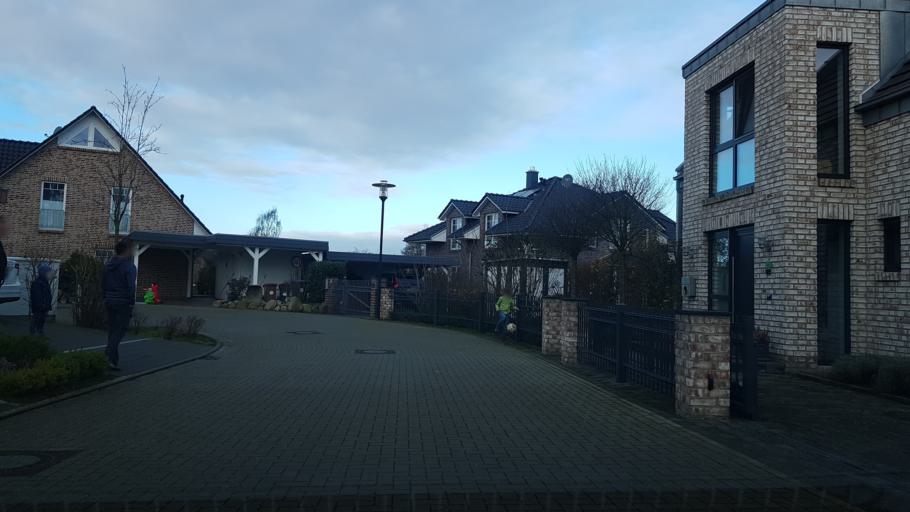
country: DE
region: Lower Saxony
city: Bardowick
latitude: 53.2767
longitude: 10.3927
